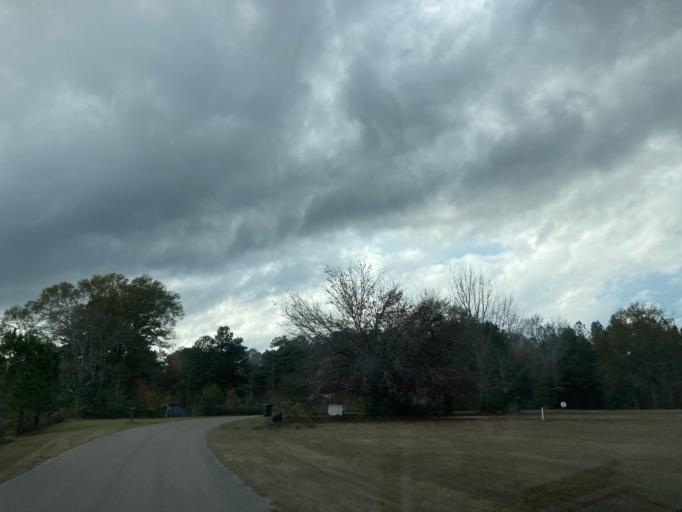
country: US
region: Mississippi
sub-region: Lamar County
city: Purvis
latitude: 31.1638
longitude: -89.6170
